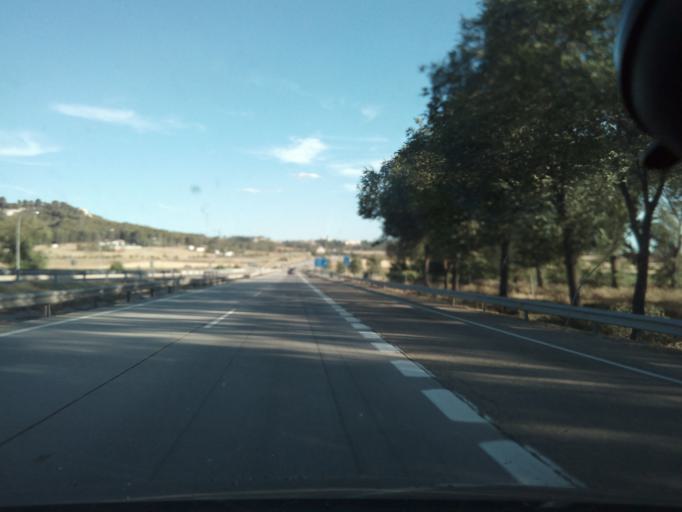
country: ES
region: Castille-La Mancha
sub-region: Province of Toledo
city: Dosbarrios
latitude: 39.8122
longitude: -3.4795
